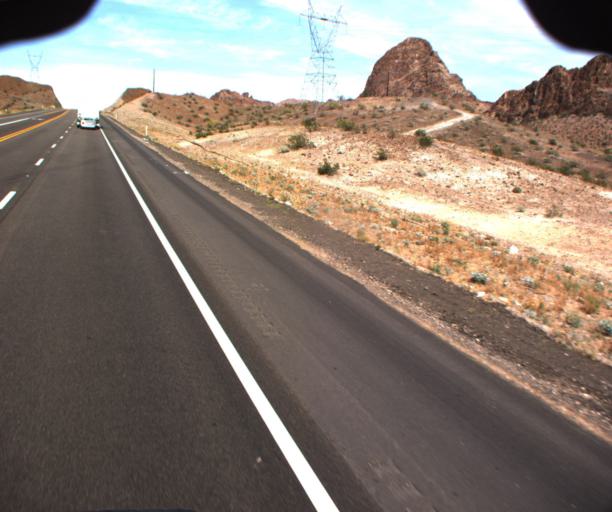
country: US
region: Arizona
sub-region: Mohave County
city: Desert Hills
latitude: 34.6103
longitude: -114.3550
